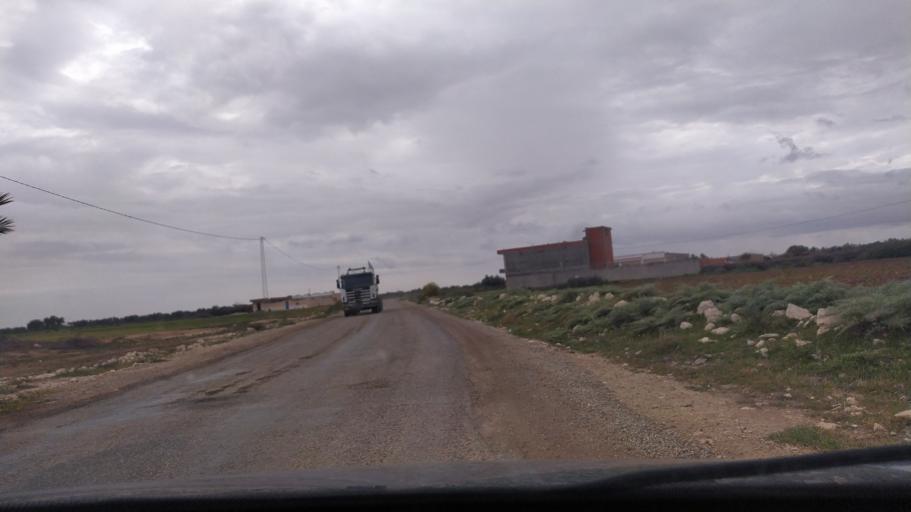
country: TN
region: Al Munastir
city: Sidi Bin Nur
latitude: 35.5074
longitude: 10.9614
